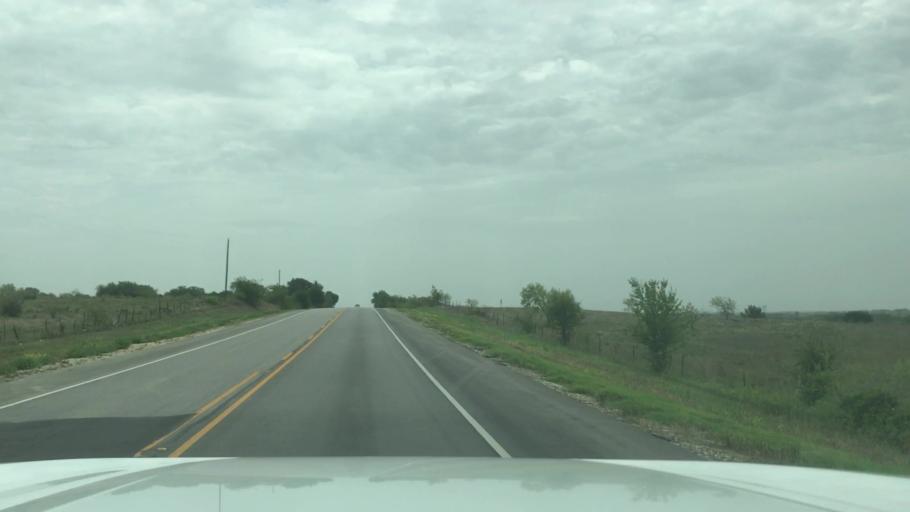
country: US
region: Texas
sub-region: Erath County
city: Dublin
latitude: 32.0814
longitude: -98.2458
